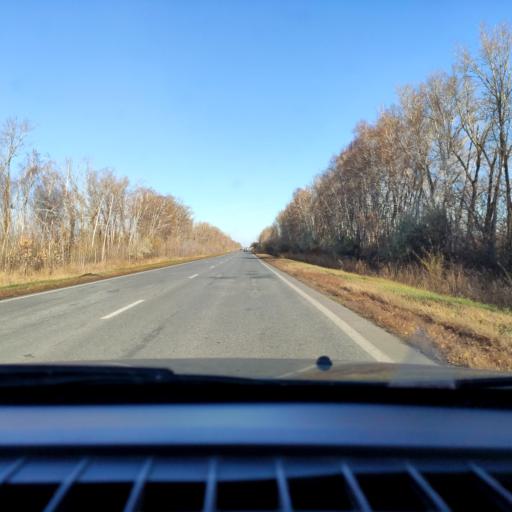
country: RU
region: Samara
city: Tol'yatti
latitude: 53.6095
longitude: 49.3169
